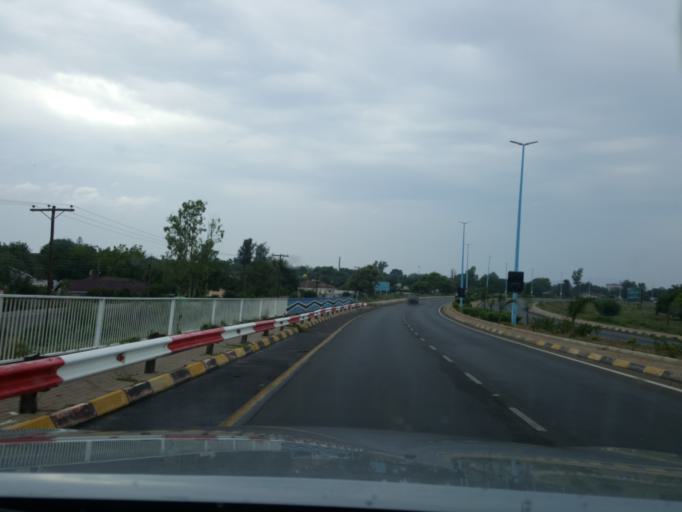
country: BW
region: South East
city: Gaborone
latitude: -24.6147
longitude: 25.9290
